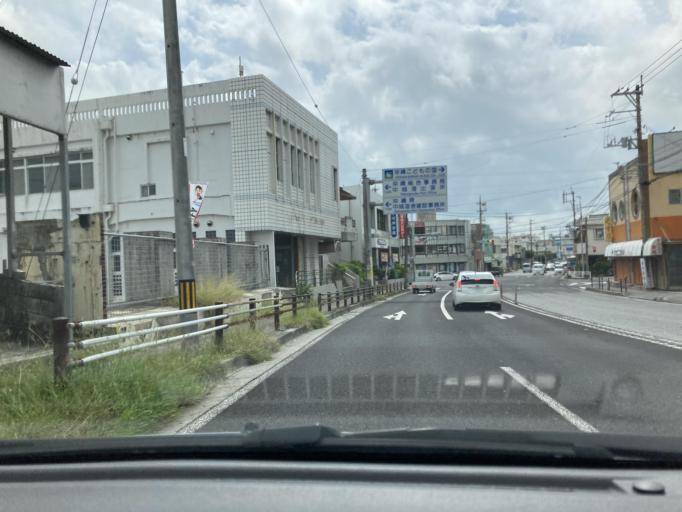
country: JP
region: Okinawa
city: Okinawa
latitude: 26.3260
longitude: 127.8230
